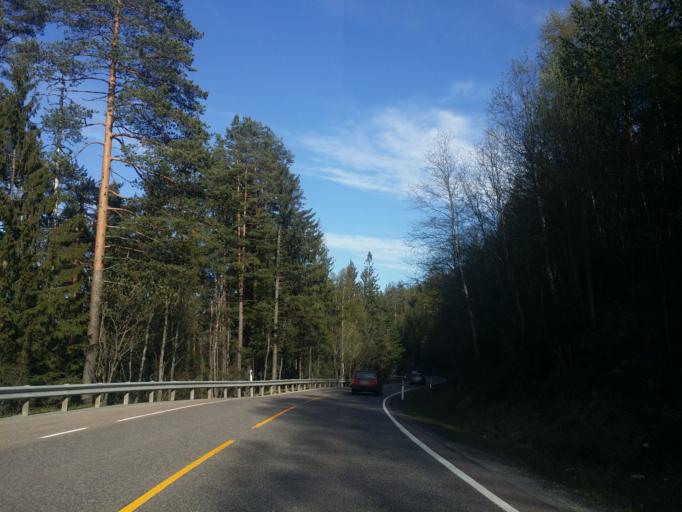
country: NO
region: Buskerud
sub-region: Kongsberg
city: Kongsberg
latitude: 59.6271
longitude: 9.5802
